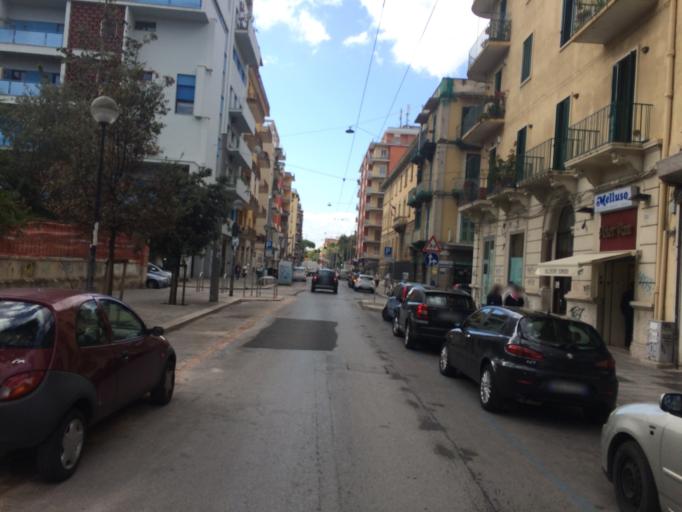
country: IT
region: Apulia
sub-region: Provincia di Bari
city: Bari
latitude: 41.1086
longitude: 16.8719
